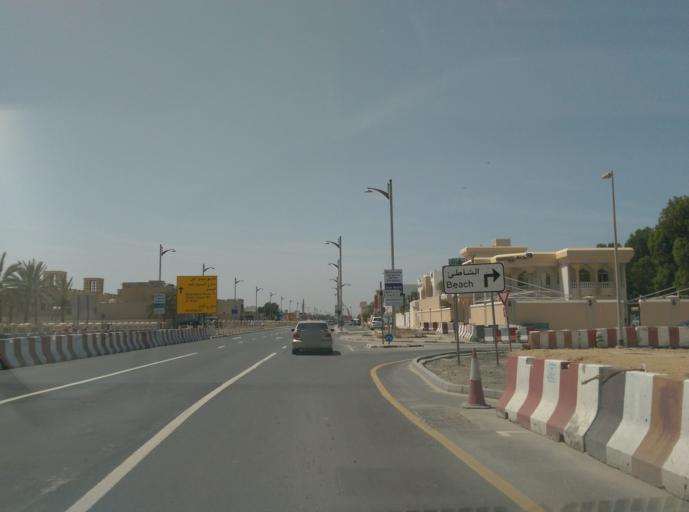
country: AE
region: Dubai
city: Dubai
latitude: 25.1920
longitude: 55.2330
